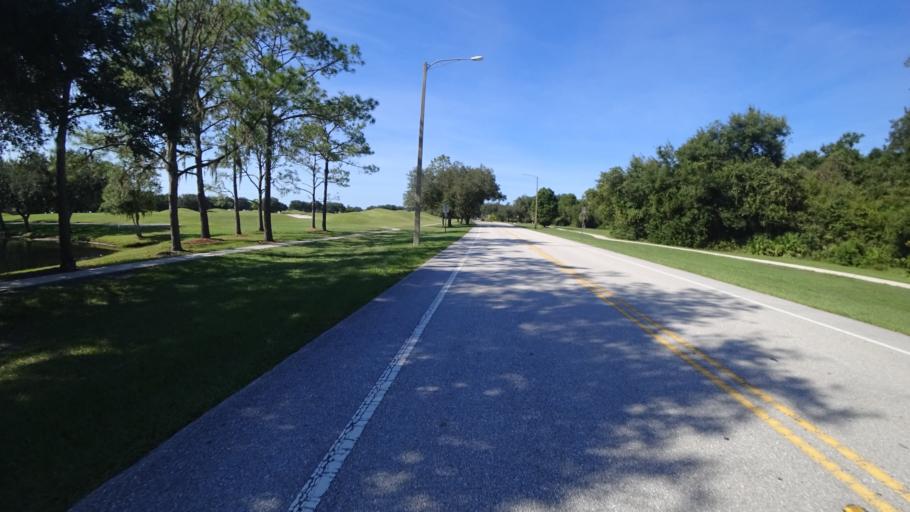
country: US
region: Florida
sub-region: Sarasota County
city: The Meadows
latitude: 27.4247
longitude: -82.4339
